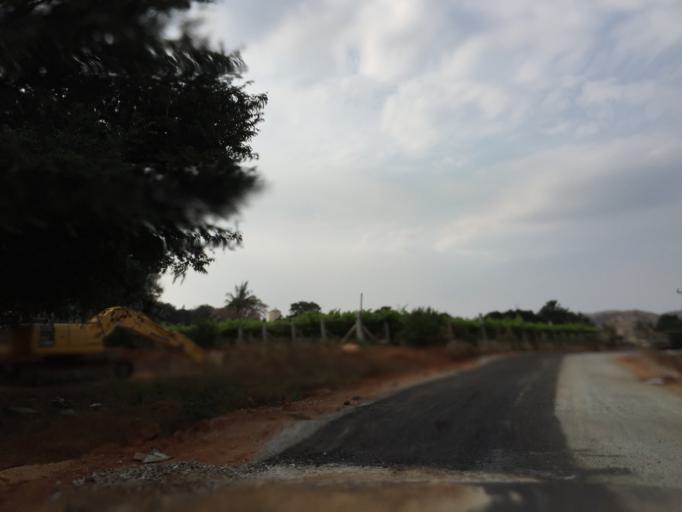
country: IN
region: Karnataka
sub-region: Chikkaballapur
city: Gudibanda
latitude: 13.5624
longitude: 77.7366
